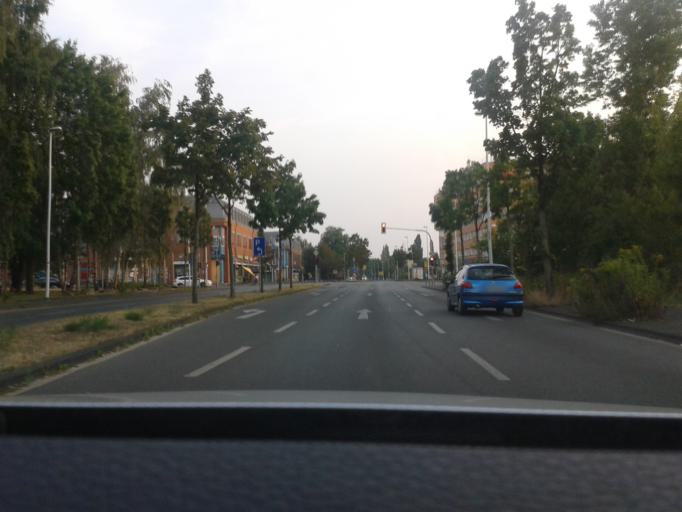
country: DE
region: Saxony
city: Albertstadt
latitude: 51.0308
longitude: 13.8034
